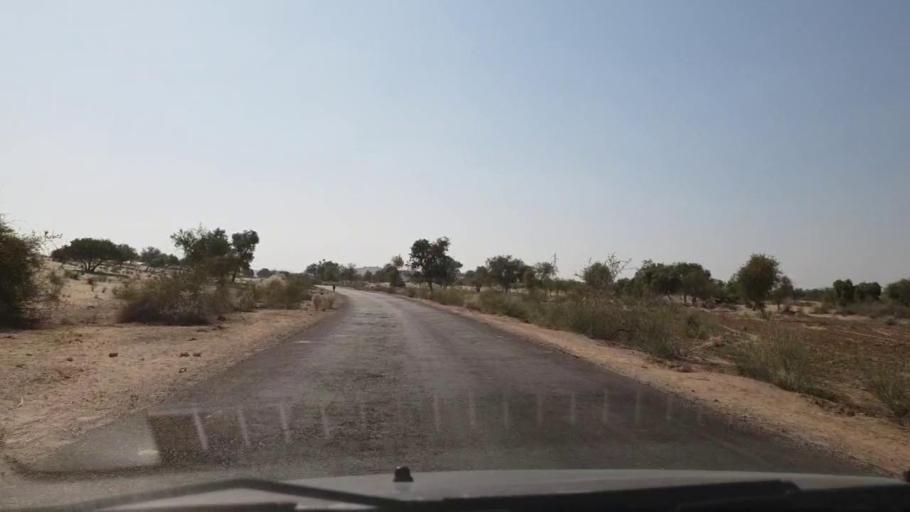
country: PK
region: Sindh
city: Mithi
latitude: 24.6609
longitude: 69.7574
